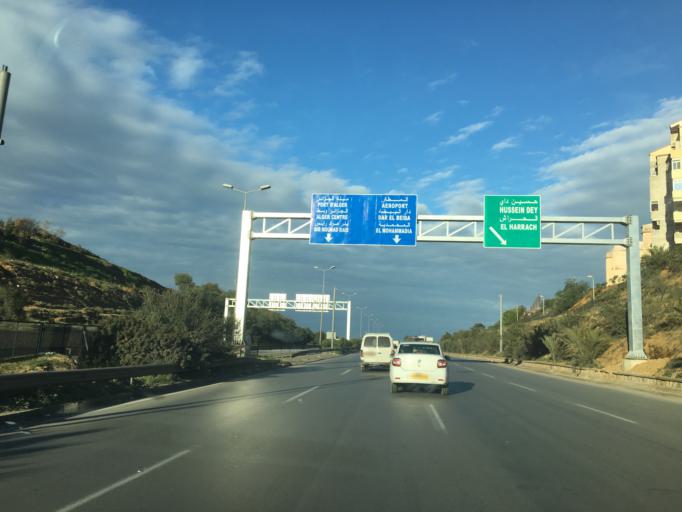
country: DZ
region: Alger
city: Bab Ezzouar
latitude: 36.7311
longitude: 3.1184
